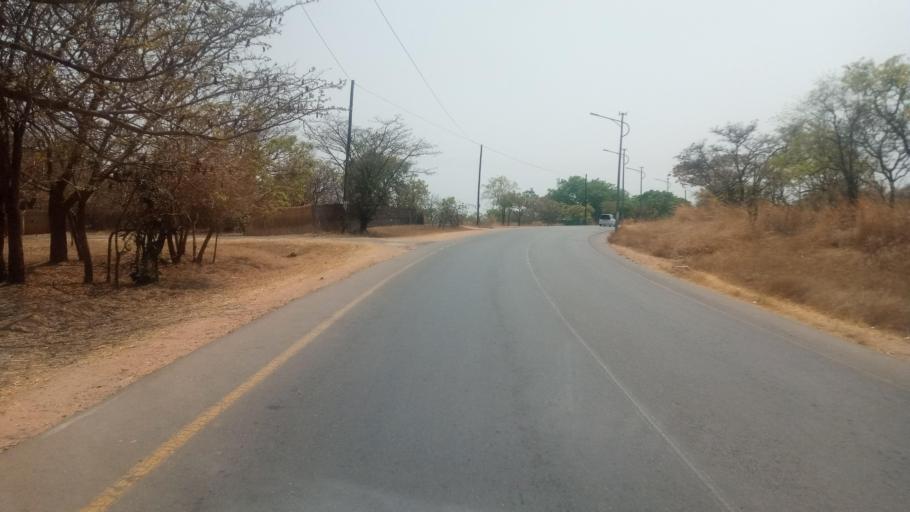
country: ZM
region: Lusaka
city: Lusaka
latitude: -15.4774
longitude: 28.4191
